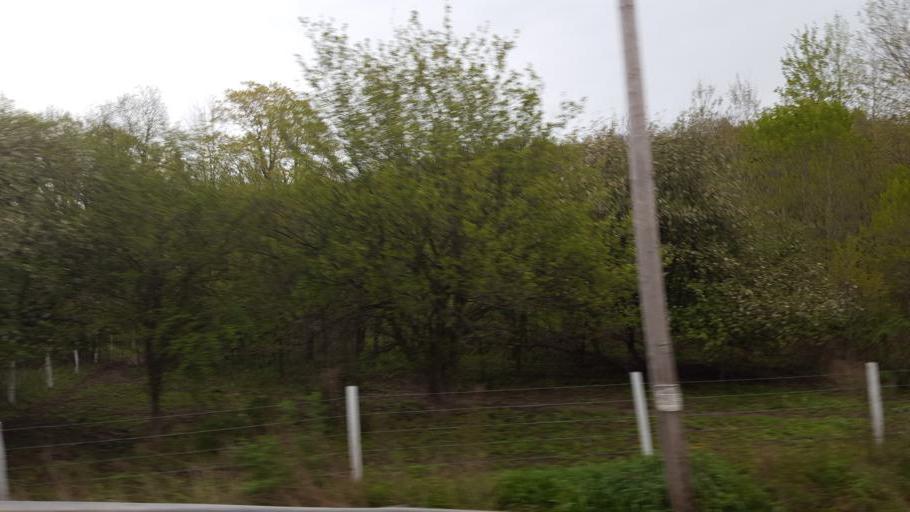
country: US
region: Pennsylvania
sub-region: Tioga County
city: Westfield
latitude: 42.0468
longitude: -77.4663
